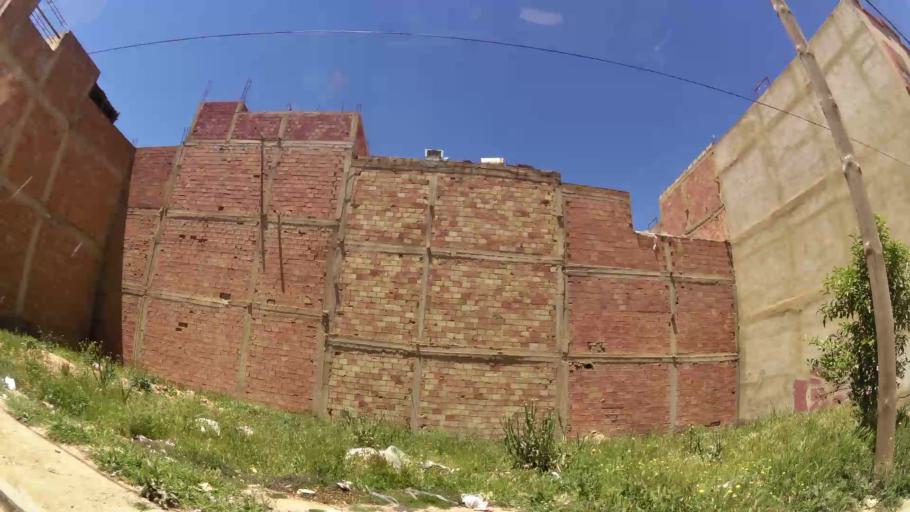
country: MA
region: Meknes-Tafilalet
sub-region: Meknes
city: Meknes
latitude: 33.8527
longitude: -5.5579
